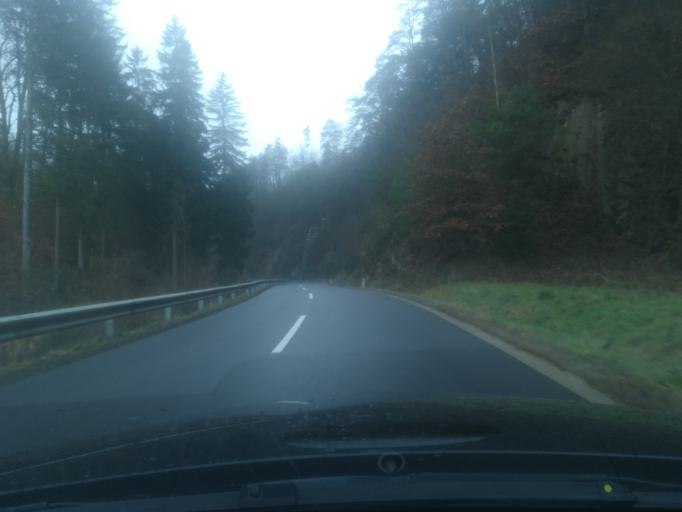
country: AT
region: Upper Austria
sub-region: Politischer Bezirk Perg
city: Perg
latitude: 48.3190
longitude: 14.5865
